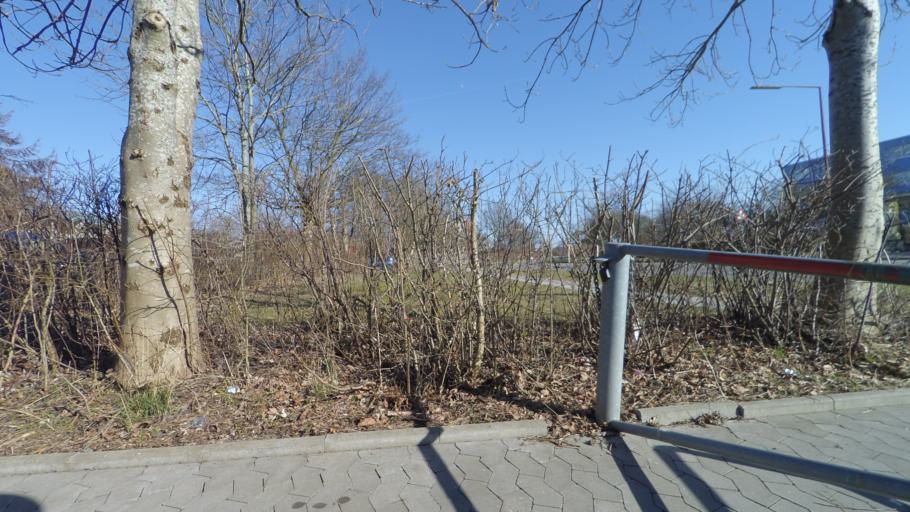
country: DK
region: Central Jutland
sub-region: Arhus Kommune
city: Arhus
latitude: 56.1673
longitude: 10.1749
